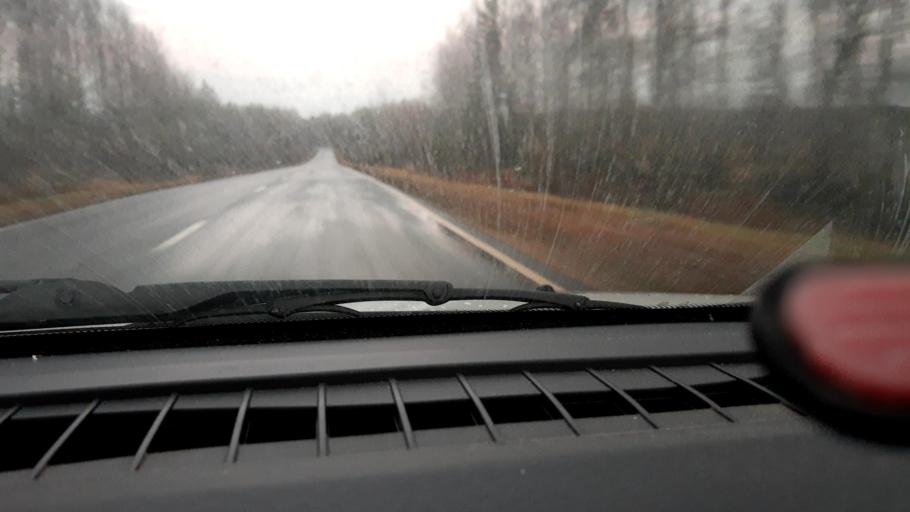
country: RU
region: Nizjnij Novgorod
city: Uren'
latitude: 57.2462
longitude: 45.5923
